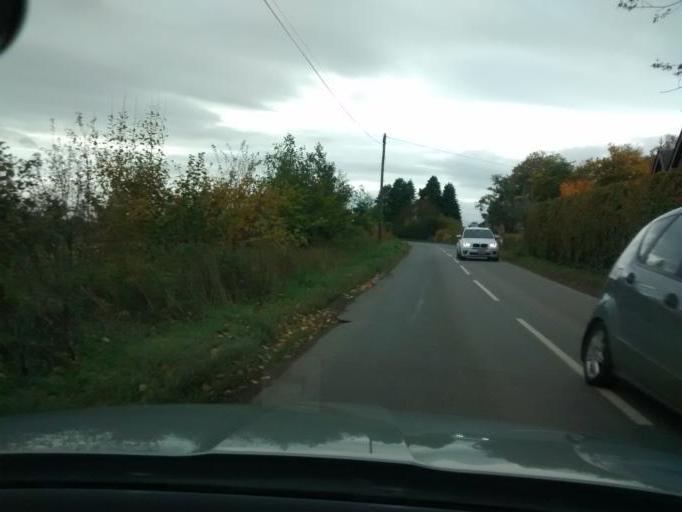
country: GB
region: Scotland
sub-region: Perth and Kinross
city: Stanley
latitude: 56.5128
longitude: -3.4092
